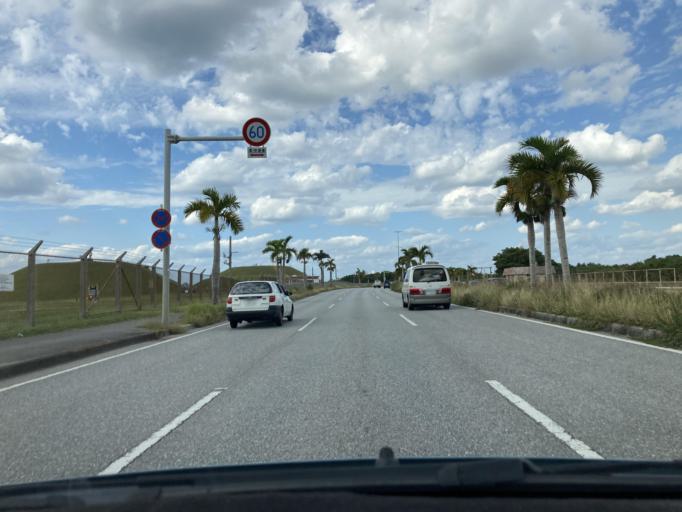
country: JP
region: Okinawa
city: Chatan
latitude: 26.3446
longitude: 127.7479
